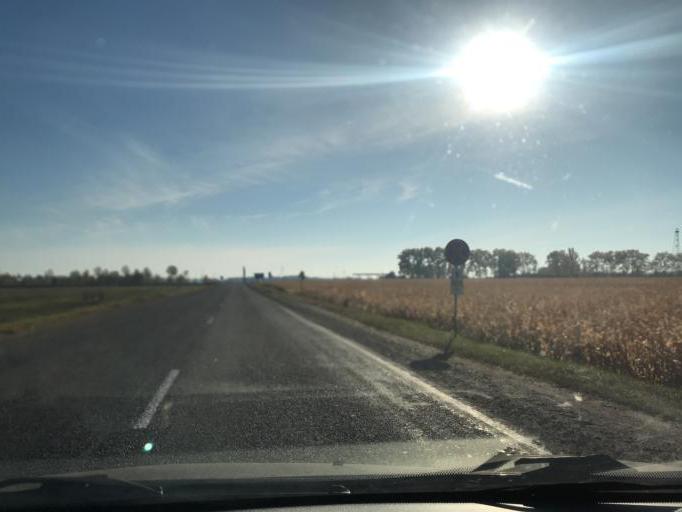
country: BY
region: Gomel
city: Brahin
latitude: 51.7778
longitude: 30.2427
